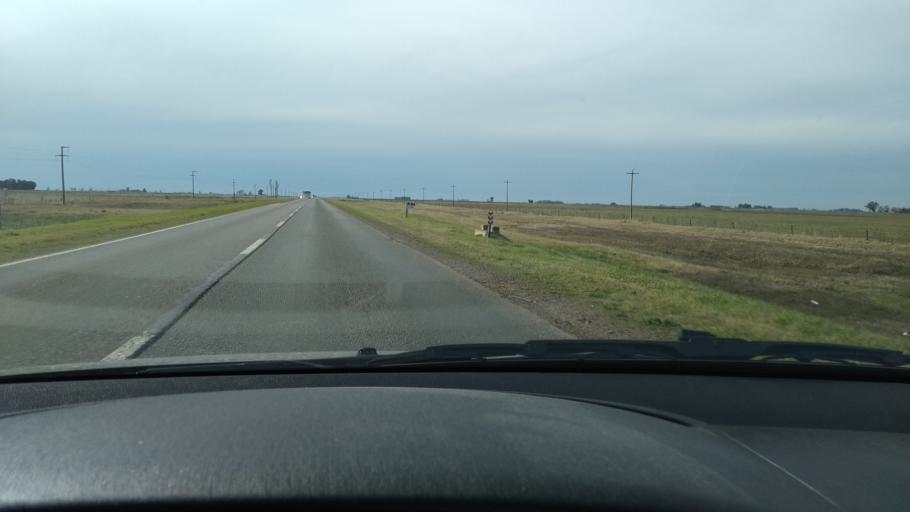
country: AR
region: Buenos Aires
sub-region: Partido de Azul
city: Azul
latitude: -36.6909
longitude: -59.7388
